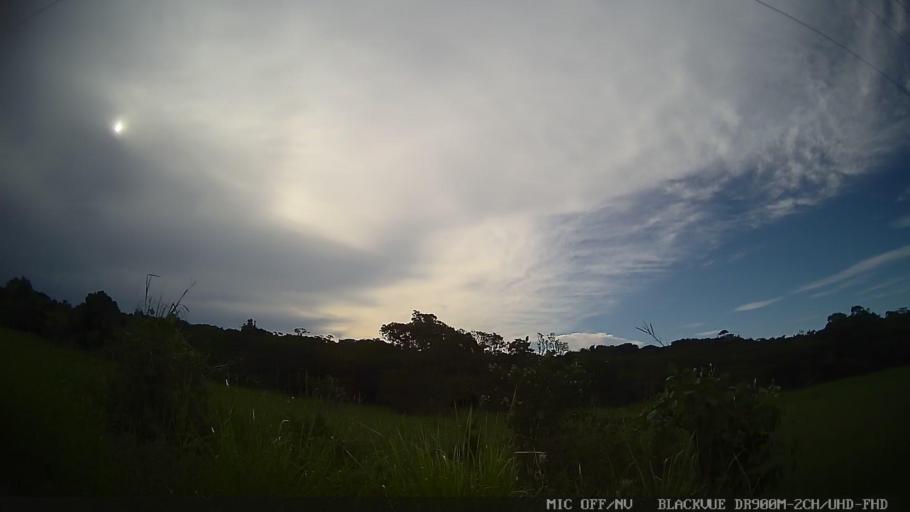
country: BR
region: Sao Paulo
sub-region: Iguape
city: Iguape
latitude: -24.6564
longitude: -47.4092
